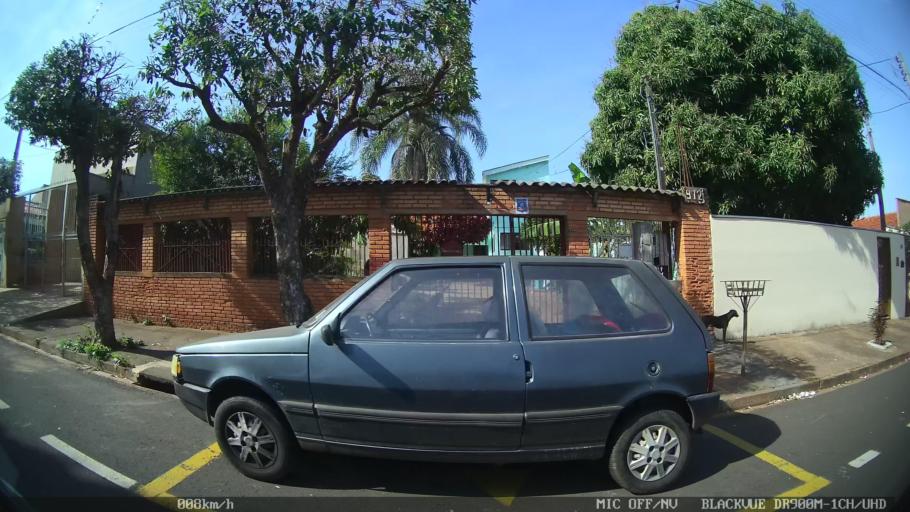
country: BR
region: Sao Paulo
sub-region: Sao Jose Do Rio Preto
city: Sao Jose do Rio Preto
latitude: -20.7991
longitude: -49.4166
